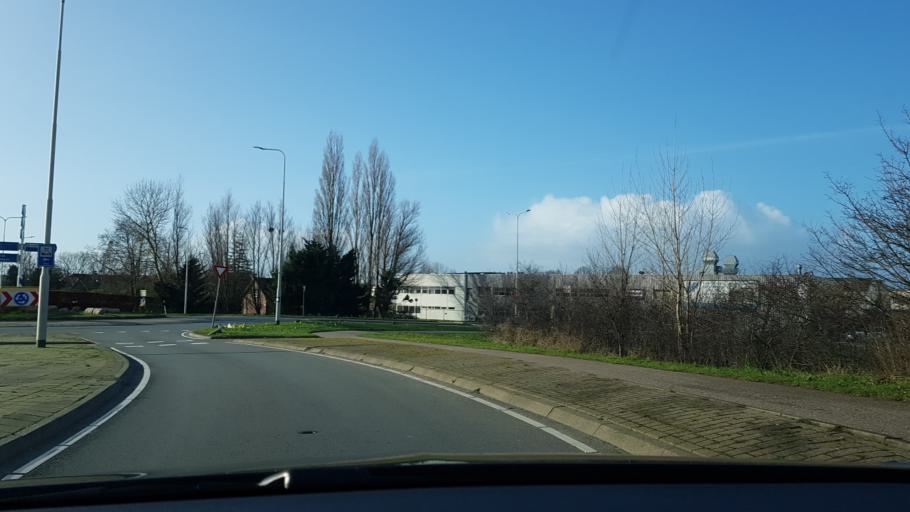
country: NL
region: South Holland
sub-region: Gemeente Teylingen
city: Sassenheim
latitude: 52.2136
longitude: 4.5059
